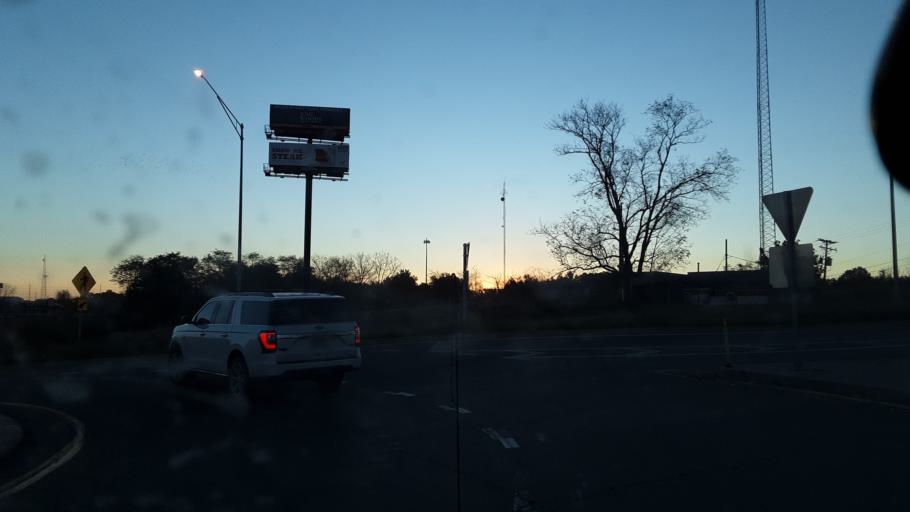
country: US
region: Missouri
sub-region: Boone County
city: Columbia
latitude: 38.9681
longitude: -92.3250
